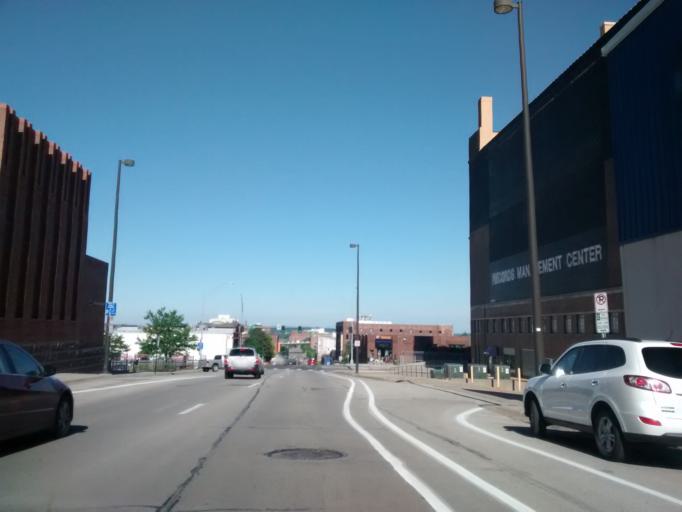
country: US
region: Nebraska
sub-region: Douglas County
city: Omaha
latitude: 41.2524
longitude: -95.9385
